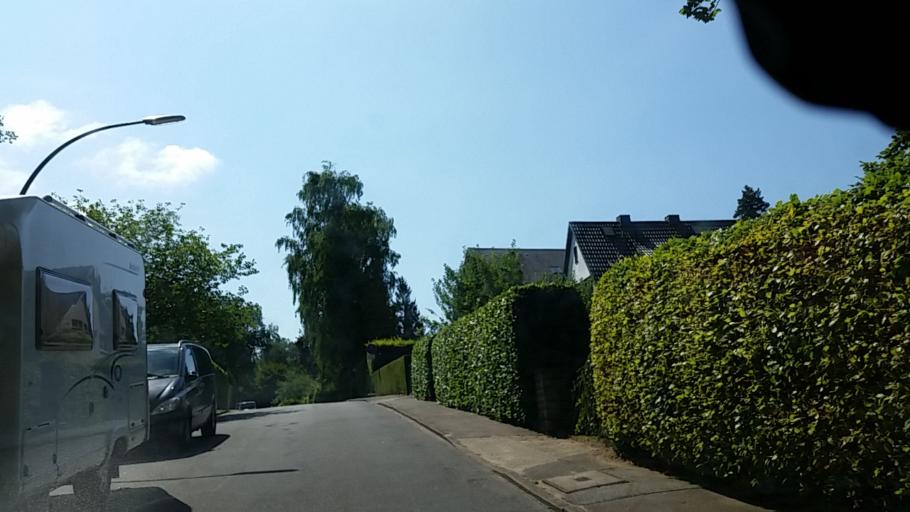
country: DE
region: Schleswig-Holstein
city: Halstenbek
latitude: 53.5738
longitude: 9.8120
